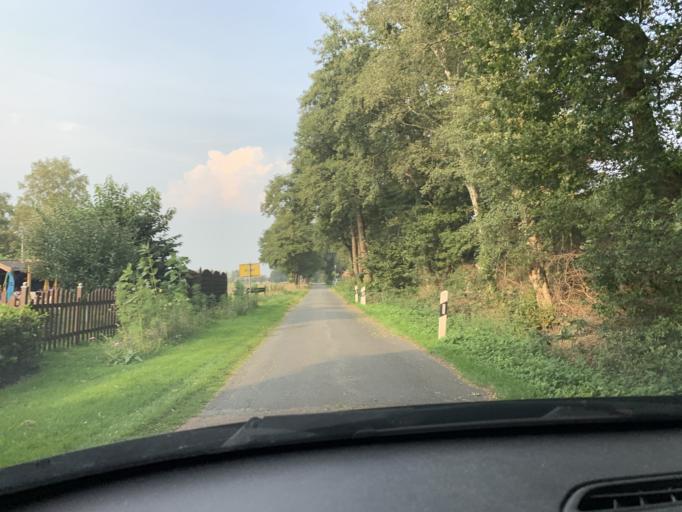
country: DE
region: Lower Saxony
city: Apen
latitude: 53.2246
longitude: 7.8169
